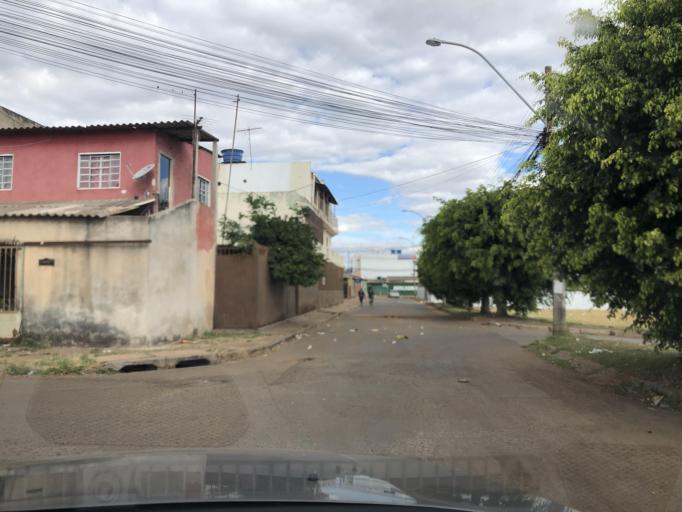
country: BR
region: Federal District
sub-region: Brasilia
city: Brasilia
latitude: -15.8887
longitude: -48.1042
